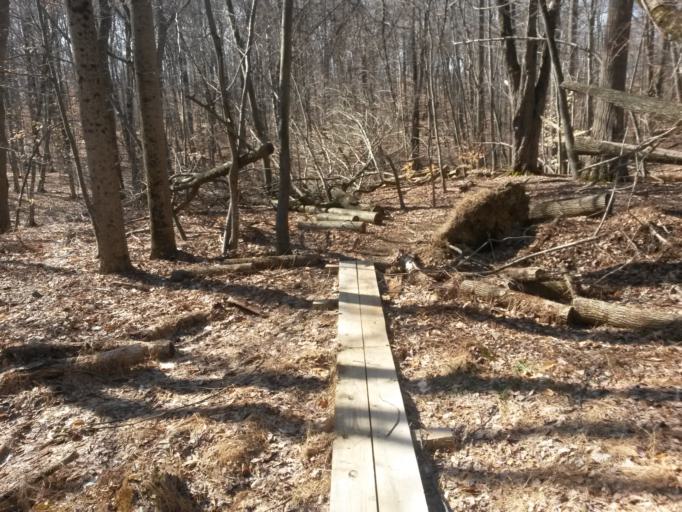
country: US
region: New York
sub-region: Westchester County
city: Yorktown Heights
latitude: 41.2496
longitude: -73.7694
